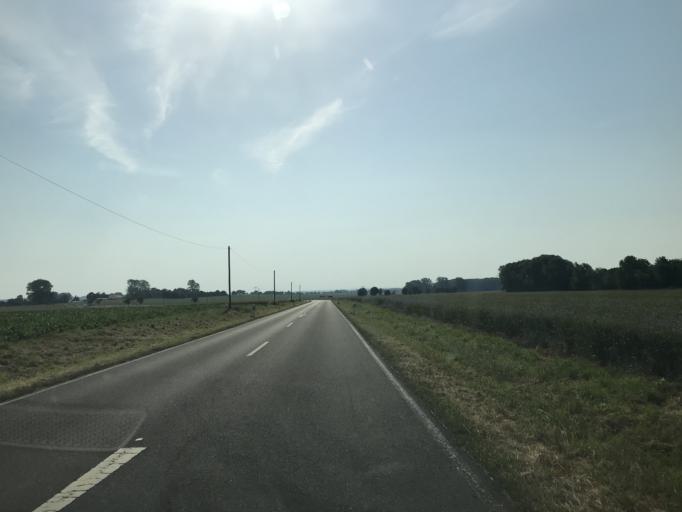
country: DE
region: Saxony-Anhalt
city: Erxleben
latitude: 52.2489
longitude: 11.2101
